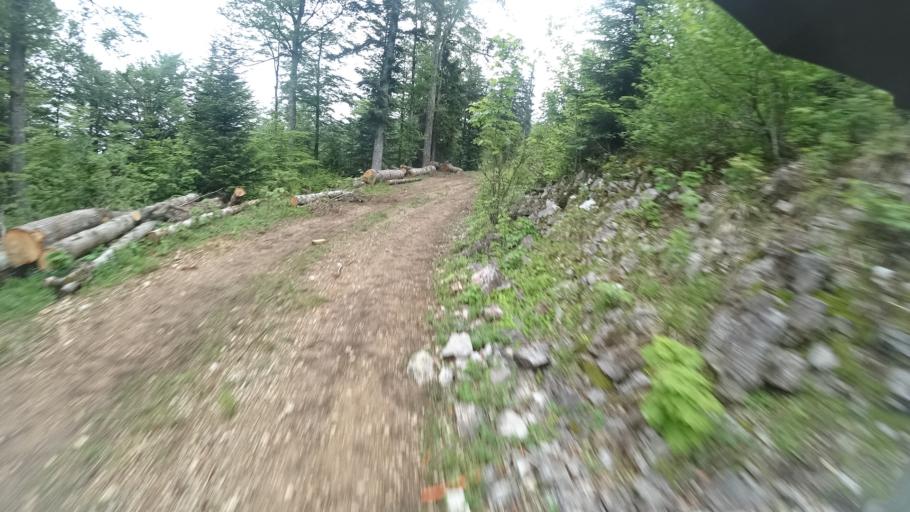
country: BA
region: Federation of Bosnia and Herzegovina
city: Bihac
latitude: 44.6284
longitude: 15.8252
